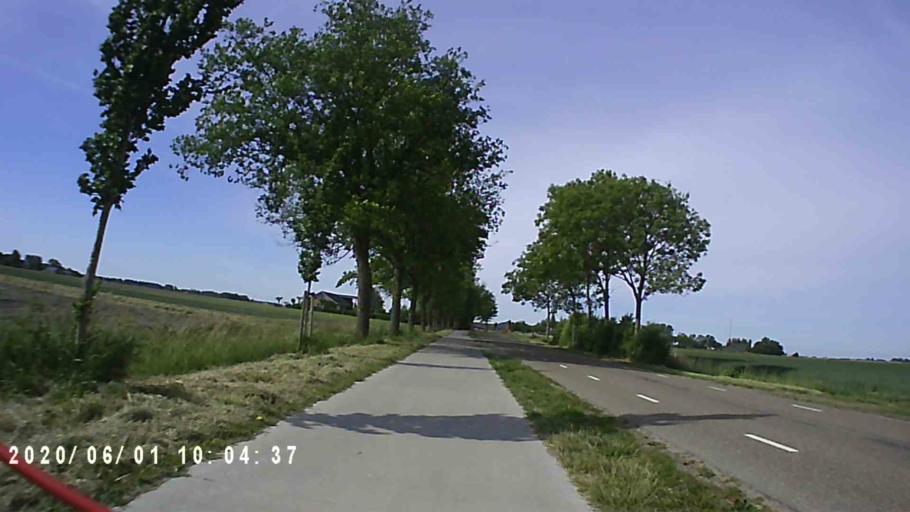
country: NL
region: Friesland
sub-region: Menameradiel
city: Berltsum
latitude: 53.2341
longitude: 5.6222
